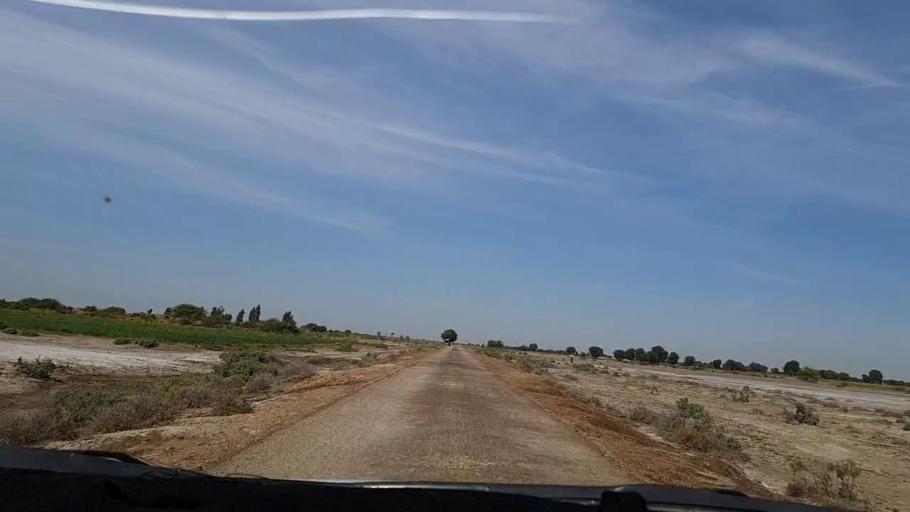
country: PK
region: Sindh
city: Pithoro
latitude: 25.4523
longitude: 69.4644
